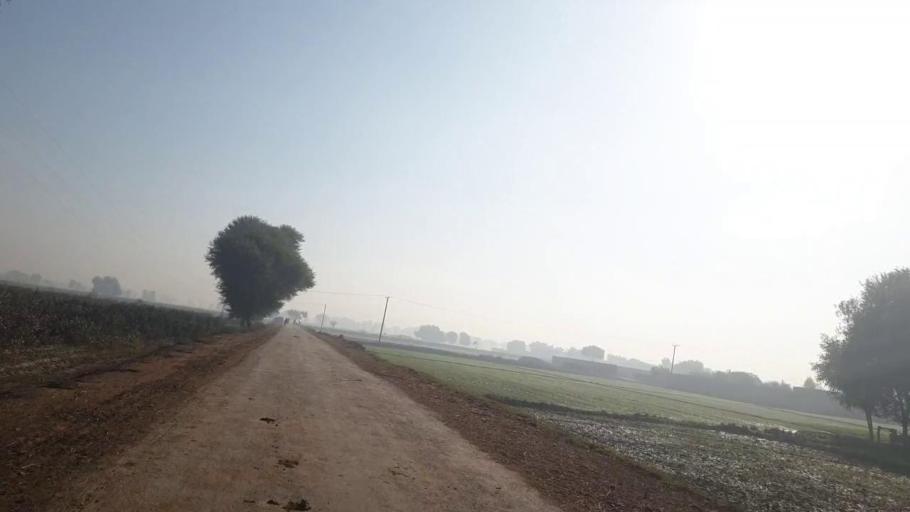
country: PK
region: Sindh
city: Dadu
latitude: 26.6752
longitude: 67.7922
